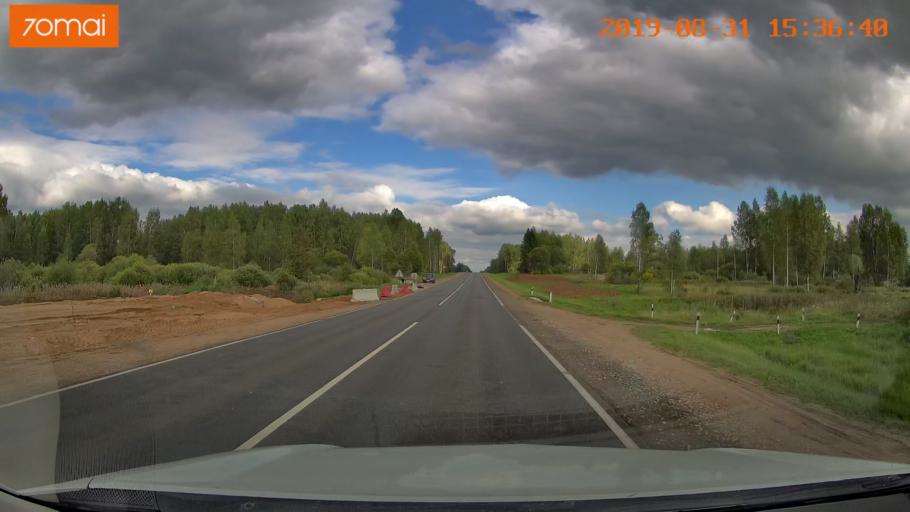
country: RU
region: Kaluga
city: Mosal'sk
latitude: 54.6127
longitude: 34.7643
